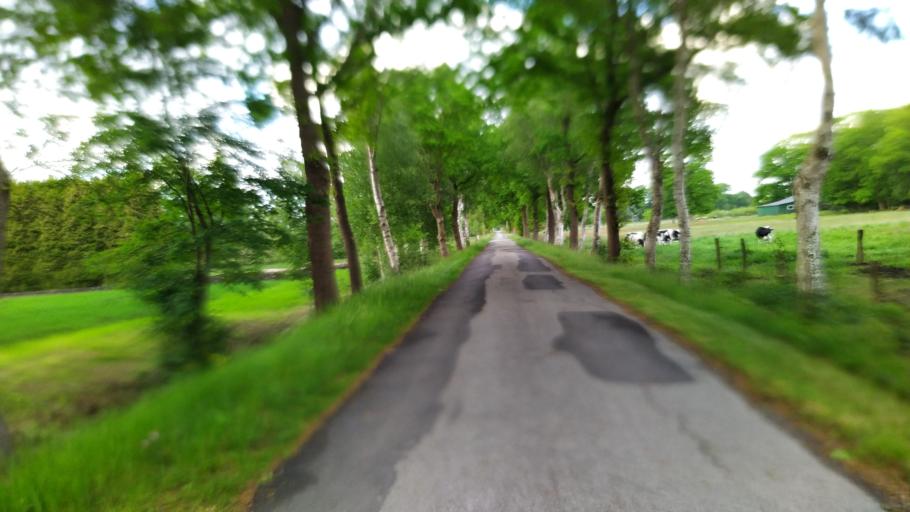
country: DE
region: Lower Saxony
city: Brest
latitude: 53.4761
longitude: 9.4119
